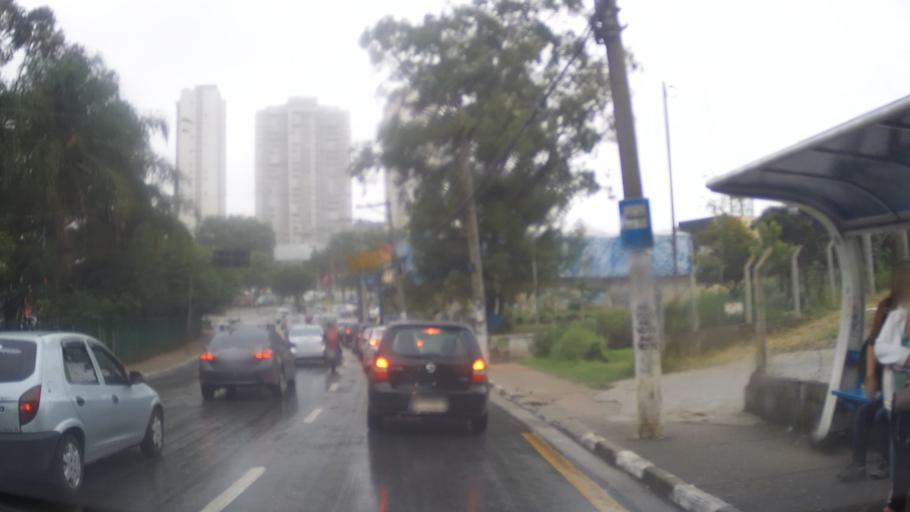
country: BR
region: Sao Paulo
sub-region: Guarulhos
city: Guarulhos
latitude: -23.4541
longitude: -46.5325
